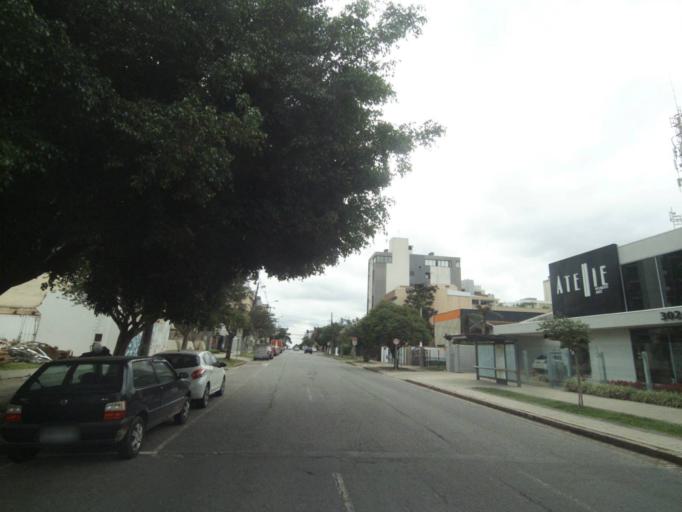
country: BR
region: Parana
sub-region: Curitiba
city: Curitiba
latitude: -25.4331
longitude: -49.2933
